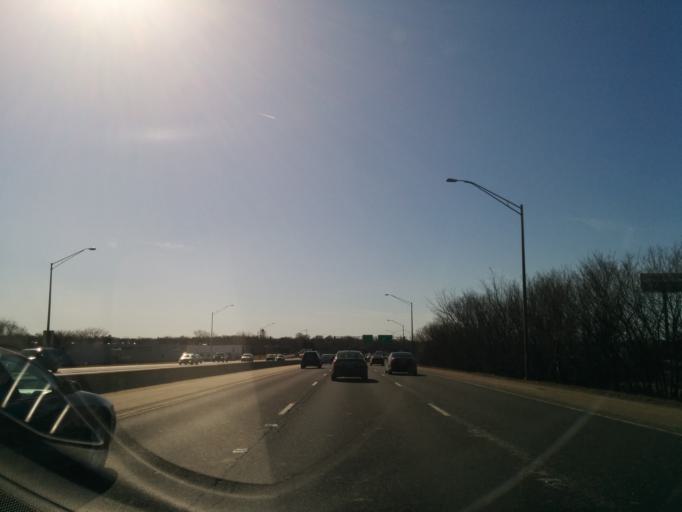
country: US
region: Illinois
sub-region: DuPage County
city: Burr Ridge
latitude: 41.7459
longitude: -87.9373
